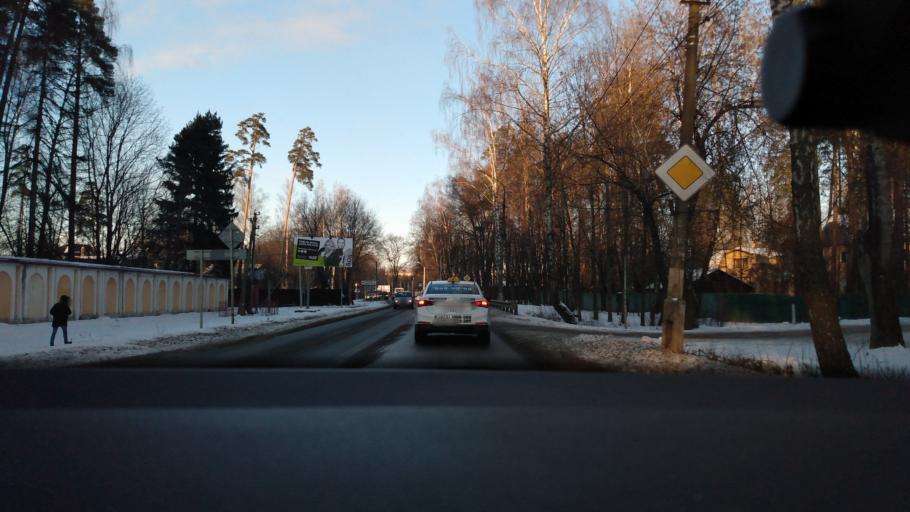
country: RU
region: Moskovskaya
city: Saltykovka
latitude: 55.7748
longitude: 37.9287
